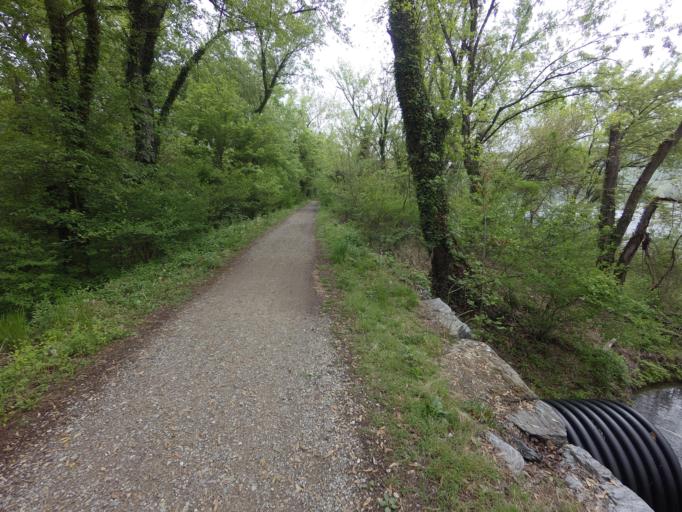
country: US
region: West Virginia
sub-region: Jefferson County
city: Bolivar
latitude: 39.3254
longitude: -77.7091
